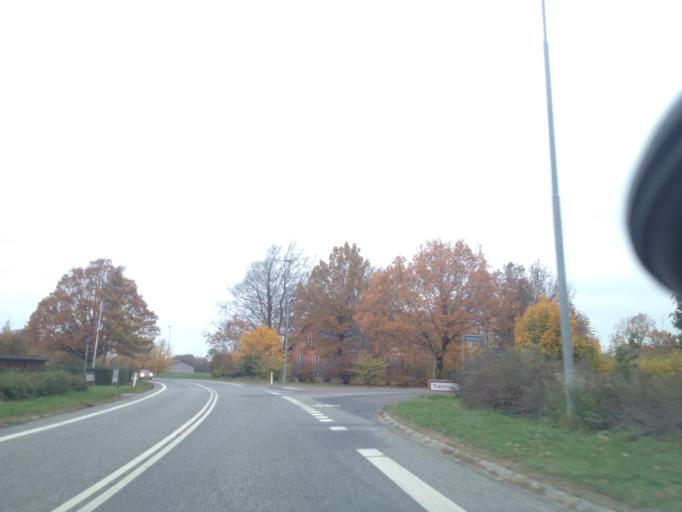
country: DK
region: South Denmark
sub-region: Nordfyns Kommune
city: Sonderso
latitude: 55.4270
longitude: 10.2542
